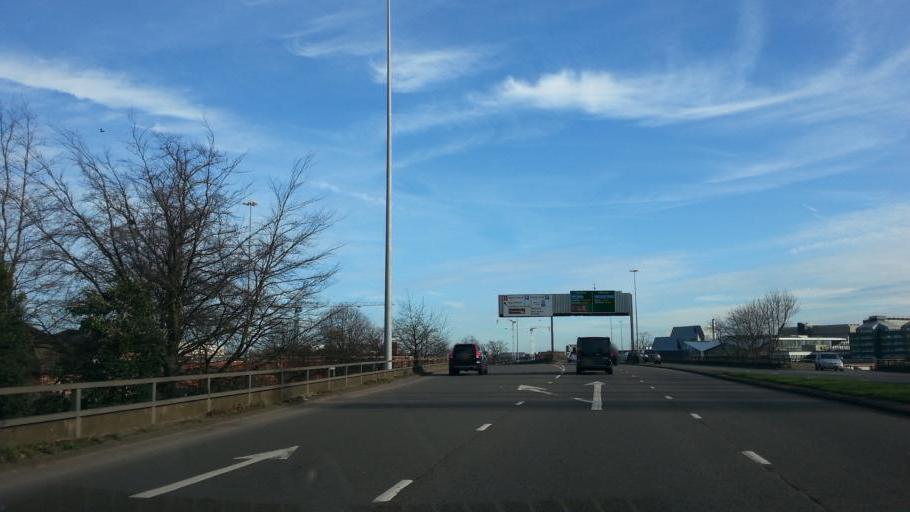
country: GB
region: England
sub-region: Coventry
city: Coventry
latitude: 52.4123
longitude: -1.5076
